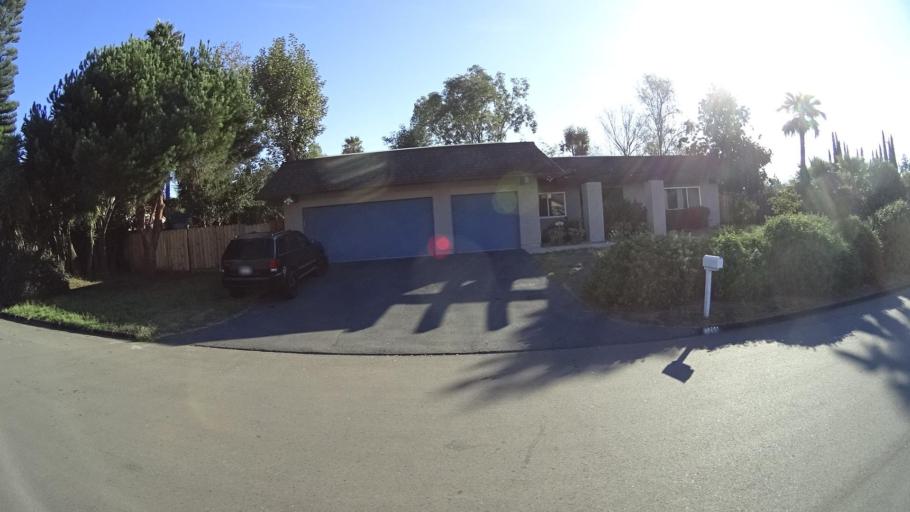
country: US
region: California
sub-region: San Diego County
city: Bonita
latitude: 32.6738
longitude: -117.0319
